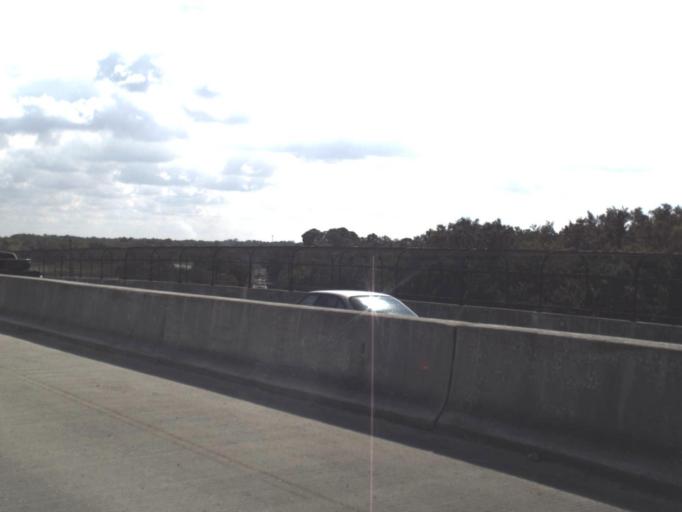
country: US
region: Florida
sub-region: Polk County
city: Medulla
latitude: 27.9965
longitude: -81.9824
